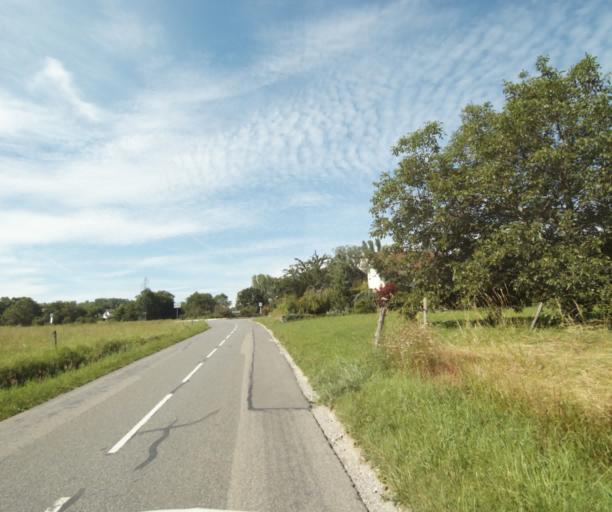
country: FR
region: Rhone-Alpes
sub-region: Departement de la Haute-Savoie
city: Margencel
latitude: 46.3330
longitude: 6.4180
